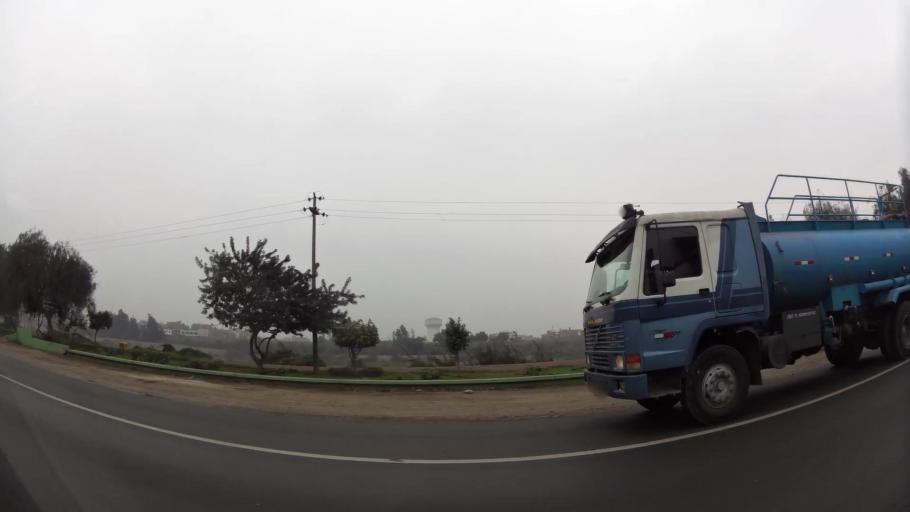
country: PE
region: Lima
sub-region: Lima
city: Vitarte
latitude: -12.0213
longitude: -76.9303
